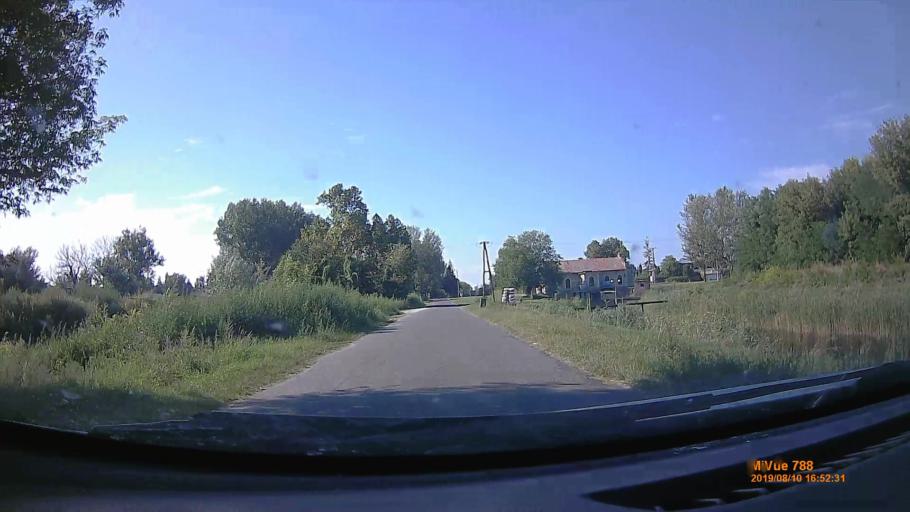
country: HU
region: Somogy
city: Balatonfenyves
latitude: 46.7068
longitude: 17.4810
